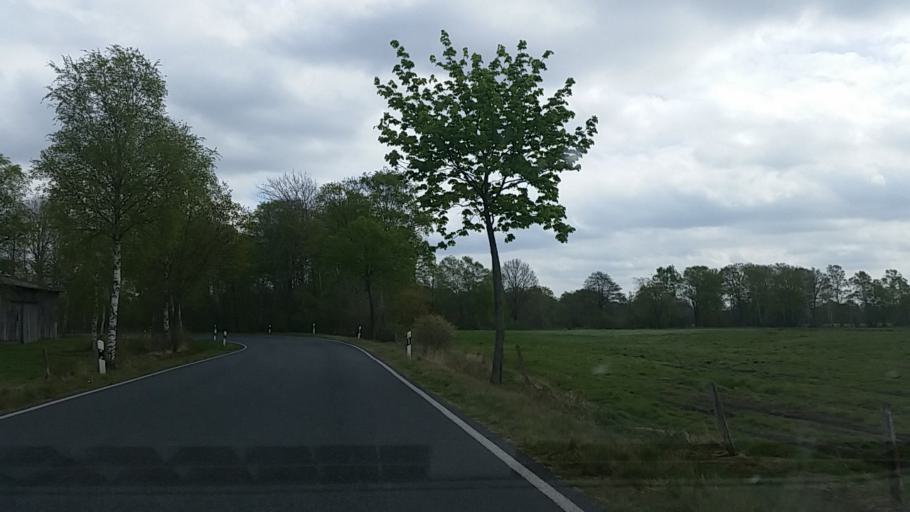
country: DE
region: Lower Saxony
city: Otter
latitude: 53.2194
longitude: 9.7204
